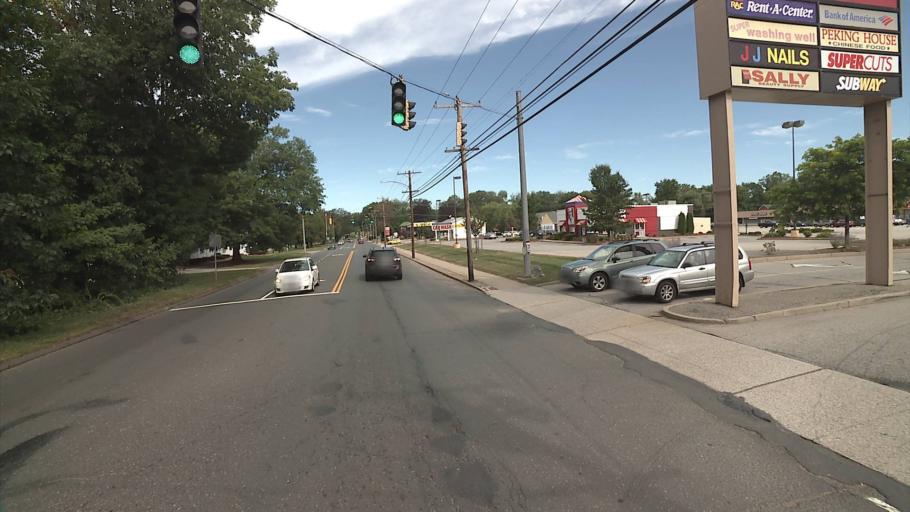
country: US
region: Connecticut
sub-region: Windham County
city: Willimantic
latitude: 41.7221
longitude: -72.2386
